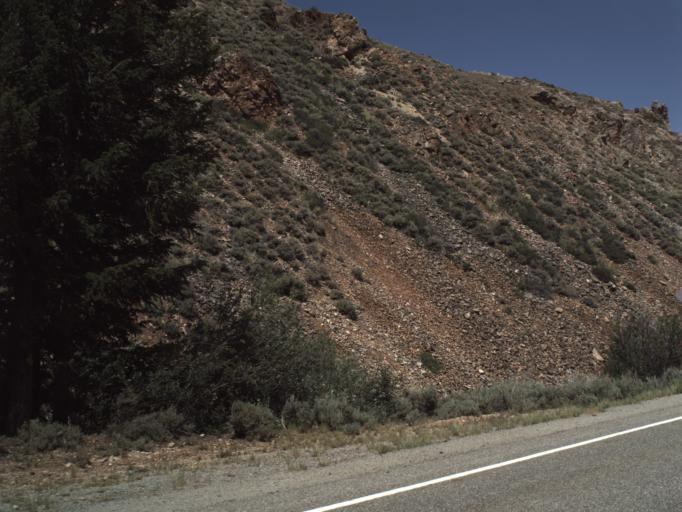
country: US
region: Utah
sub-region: Rich County
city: Randolph
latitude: 41.4809
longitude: -111.3897
